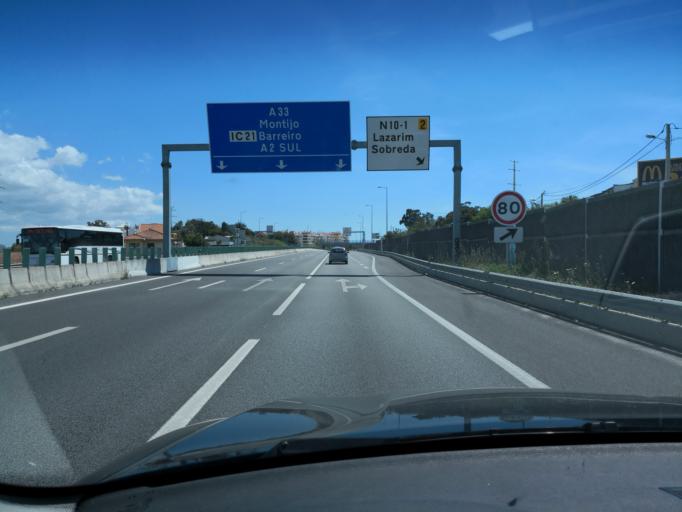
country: PT
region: Setubal
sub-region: Almada
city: Sobreda
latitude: 38.6514
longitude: -9.2011
